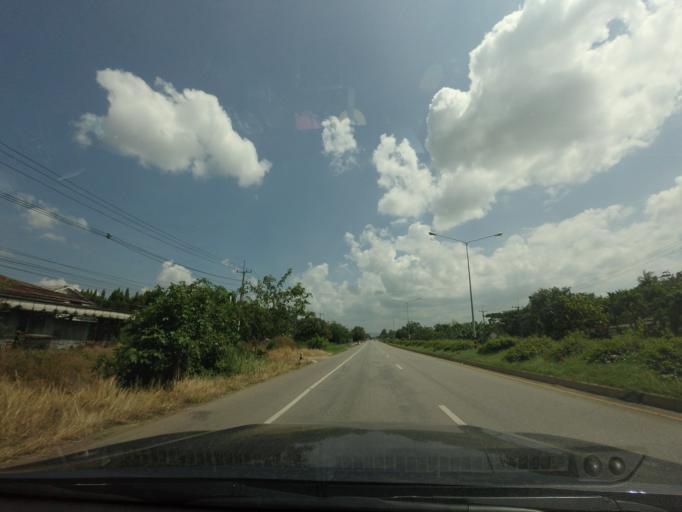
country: TH
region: Phetchabun
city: Phetchabun
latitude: 16.2578
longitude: 101.0575
